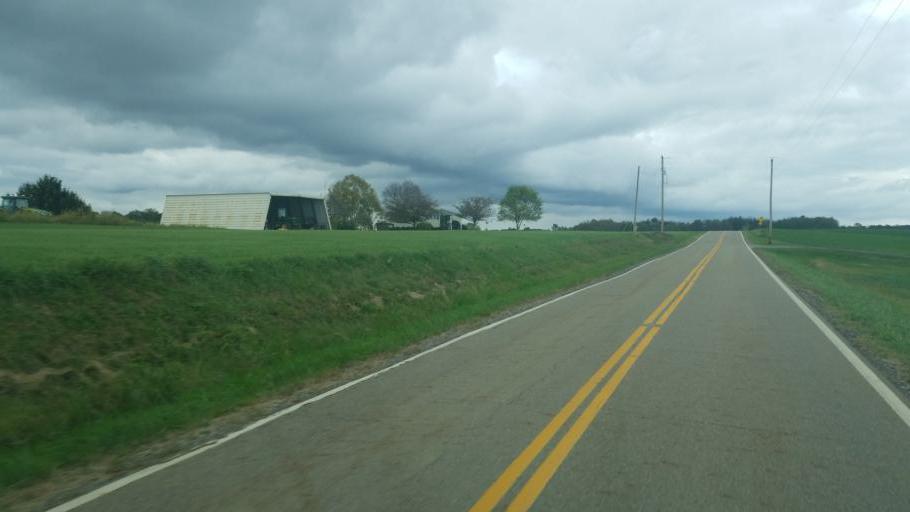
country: US
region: Ohio
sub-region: Ashland County
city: Loudonville
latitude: 40.5317
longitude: -82.1558
